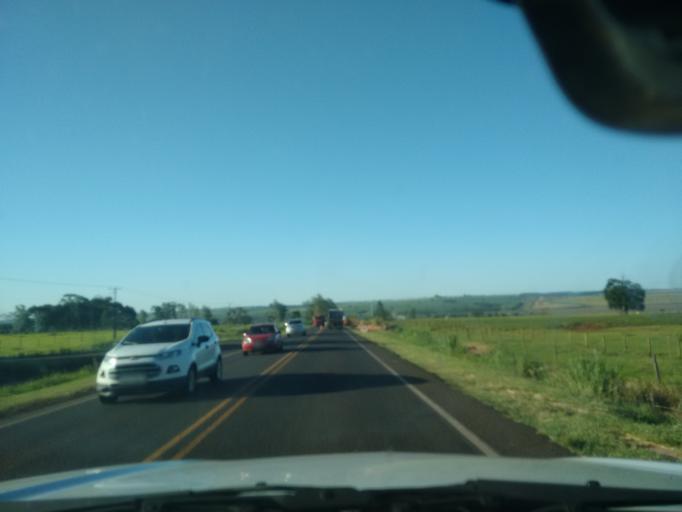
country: BR
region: Mato Grosso do Sul
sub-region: Eldorado
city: Eldorado
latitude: -23.8529
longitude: -54.3366
